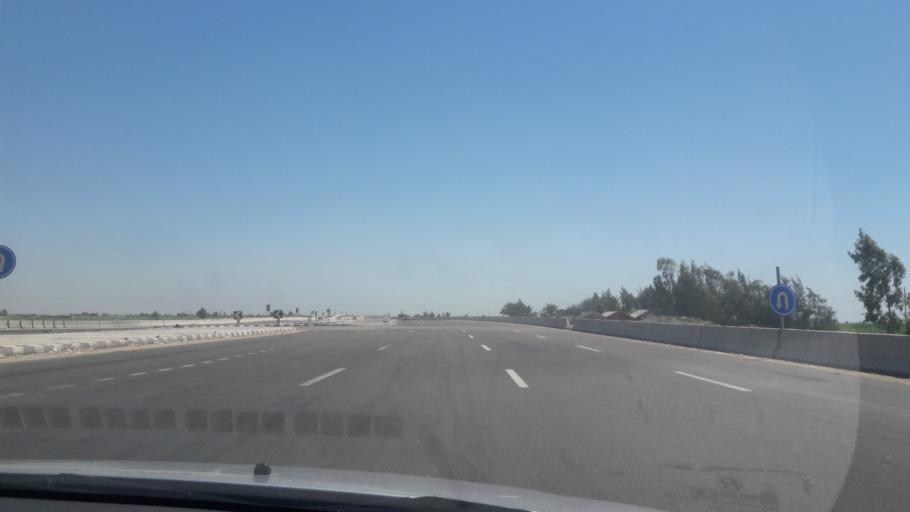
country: EG
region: Muhafazat Bur Sa`id
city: Port Said
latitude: 31.1820
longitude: 32.2351
